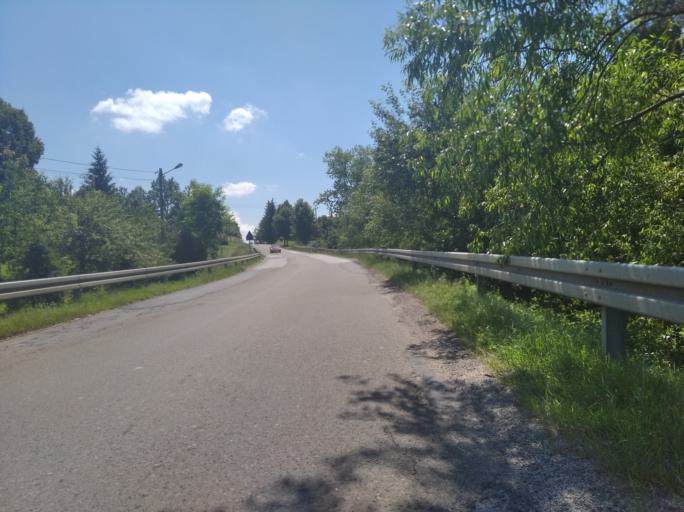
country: PL
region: Subcarpathian Voivodeship
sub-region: Powiat brzozowski
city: Jablonka
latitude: 49.6904
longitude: 22.1153
